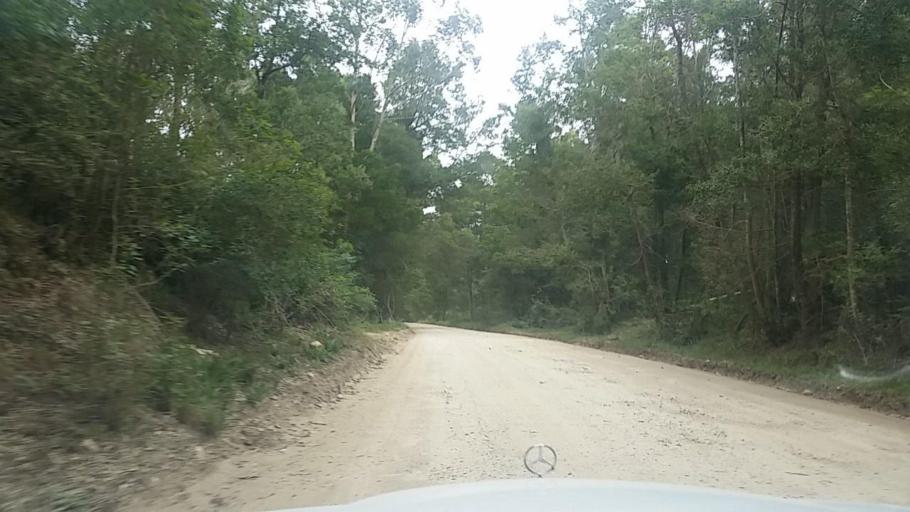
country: ZA
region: Western Cape
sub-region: Eden District Municipality
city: Knysna
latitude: -33.9923
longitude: 23.1416
